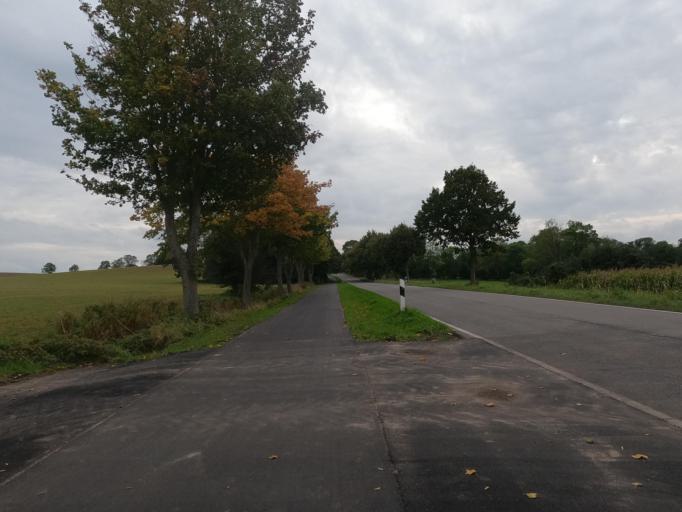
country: DE
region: Schleswig-Holstein
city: Grube
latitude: 54.2693
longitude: 11.0517
